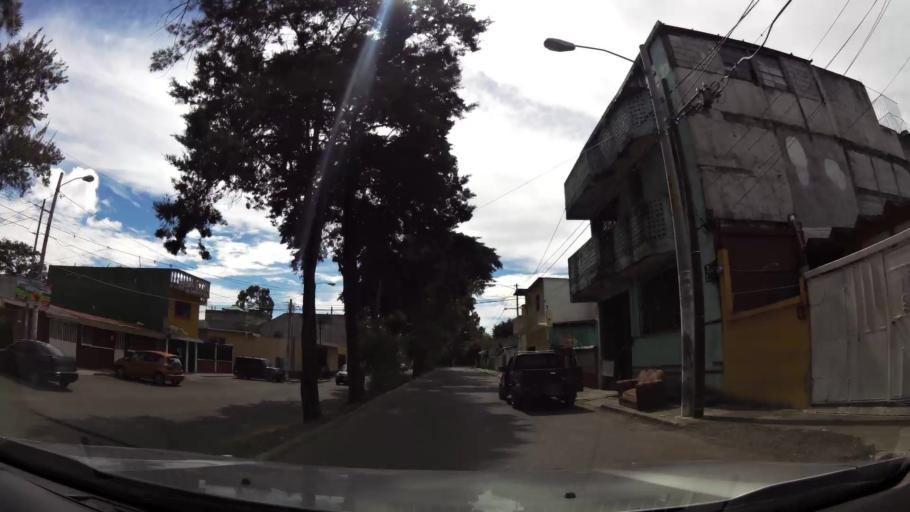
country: GT
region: Guatemala
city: Mixco
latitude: 14.6746
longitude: -90.5630
